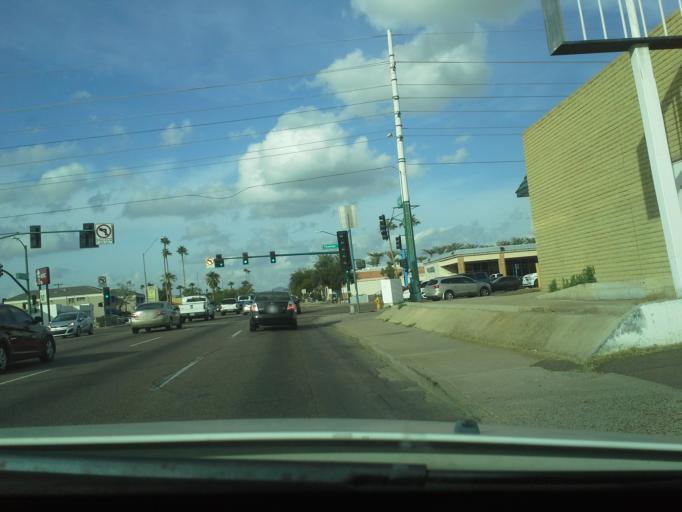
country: US
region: Arizona
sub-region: Maricopa County
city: Phoenix
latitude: 33.4798
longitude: -112.0829
